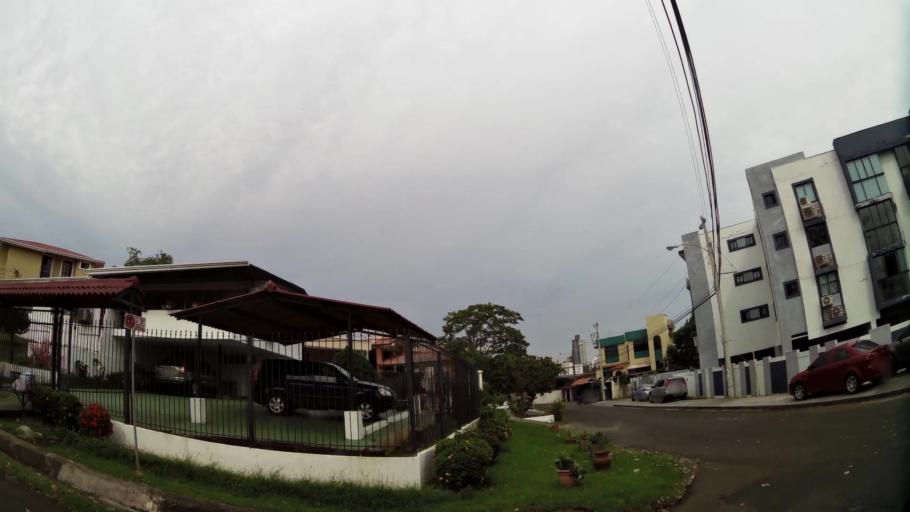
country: PA
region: Panama
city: Panama
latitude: 9.0135
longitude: -79.5197
